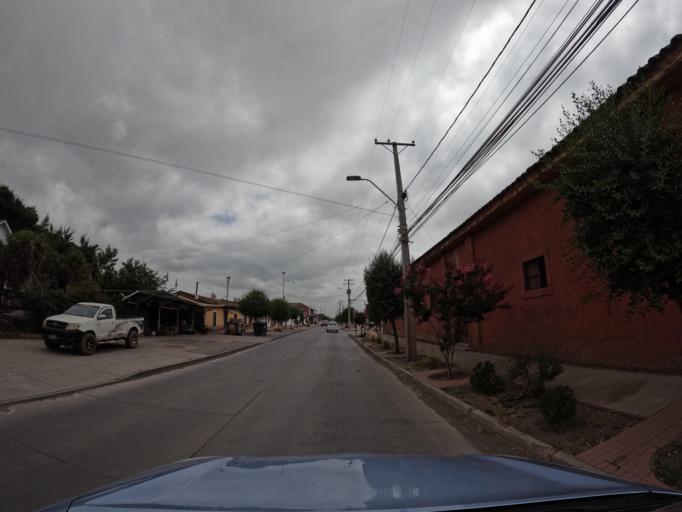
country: CL
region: O'Higgins
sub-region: Provincia de Colchagua
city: Chimbarongo
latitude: -34.7146
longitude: -71.0478
